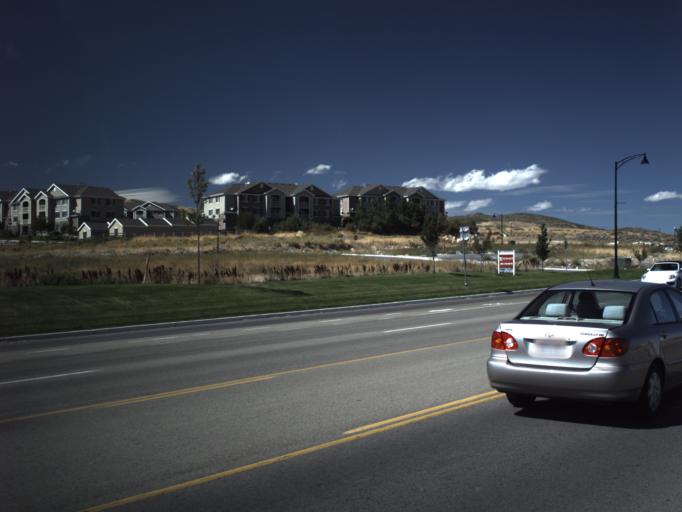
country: US
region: Utah
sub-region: Utah County
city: Saratoga Springs
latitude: 40.4003
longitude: -111.9194
